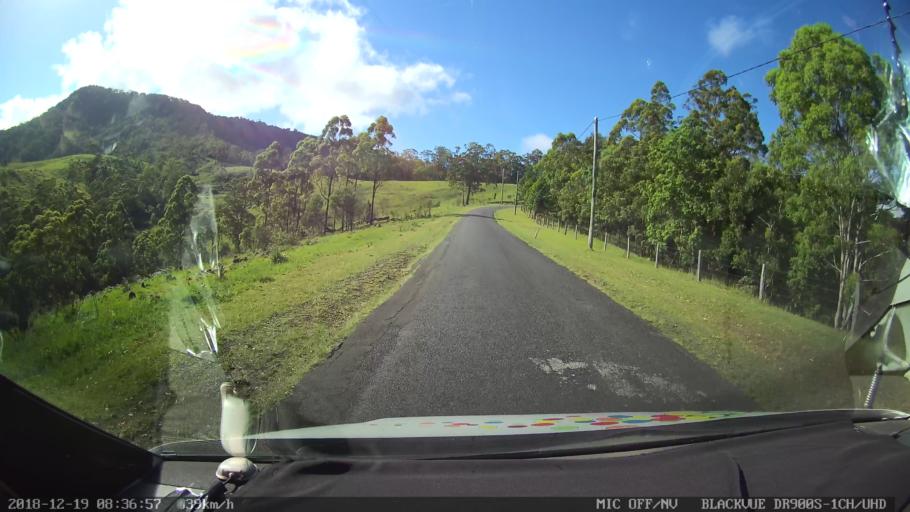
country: AU
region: New South Wales
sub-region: Kyogle
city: Kyogle
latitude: -28.3290
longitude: 152.9733
